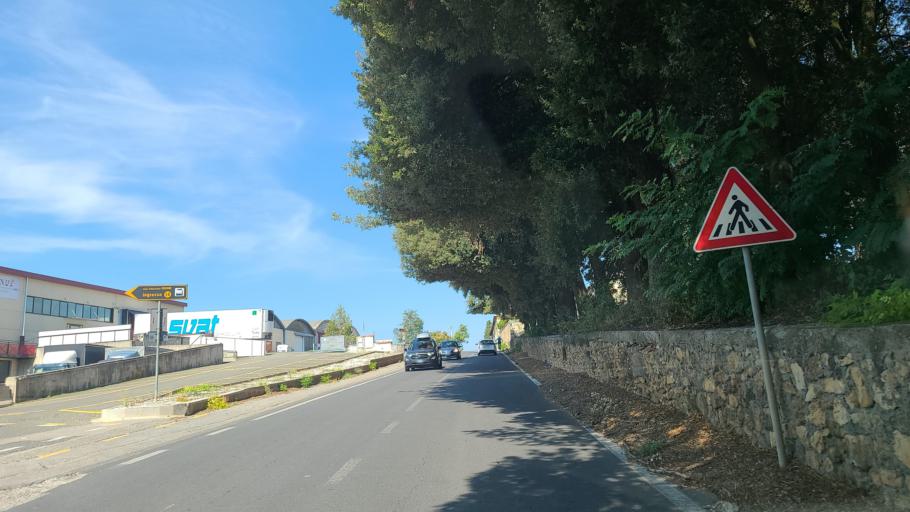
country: IT
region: Tuscany
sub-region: Provincia di Siena
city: Castellina Scalo
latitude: 43.3936
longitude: 11.1869
